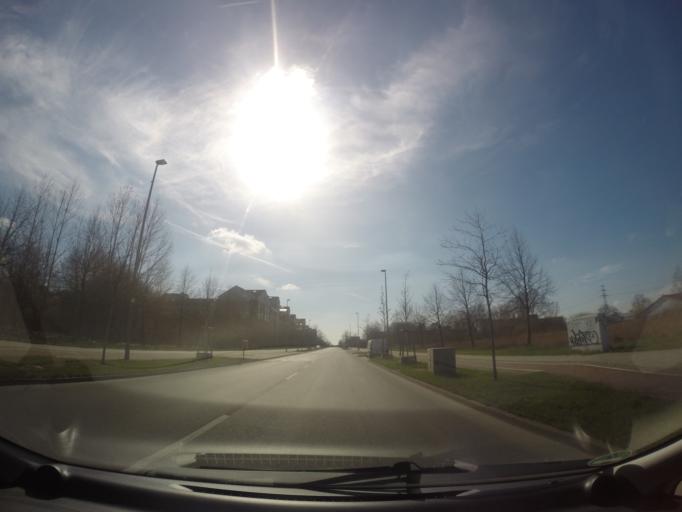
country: DE
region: Berlin
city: Falkenberg
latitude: 52.5631
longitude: 13.5533
